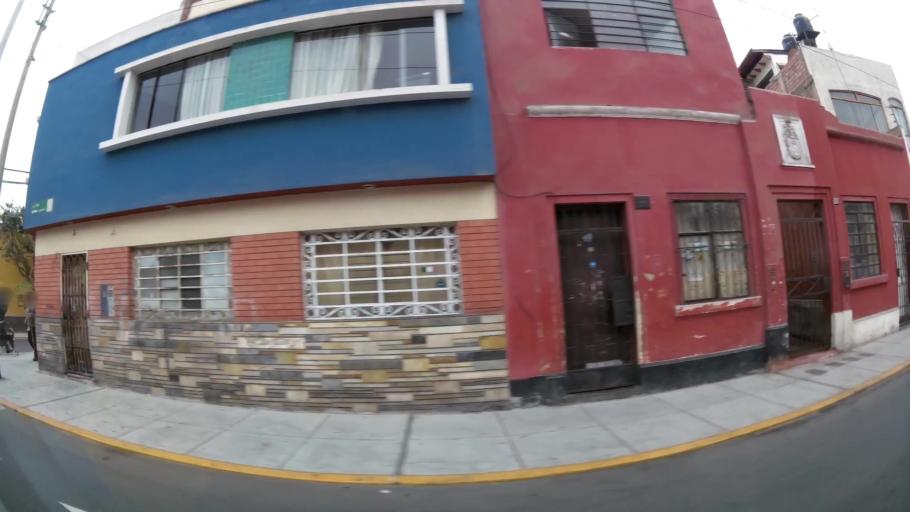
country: PE
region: Lima
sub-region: Lima
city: Surco
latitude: -12.1422
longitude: -77.0198
